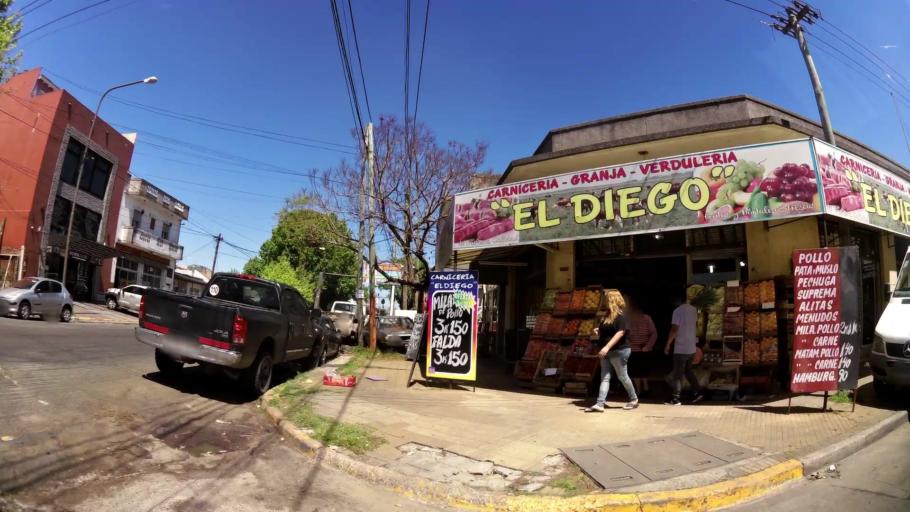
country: AR
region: Buenos Aires
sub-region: Partido de Quilmes
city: Quilmes
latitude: -34.7270
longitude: -58.2774
